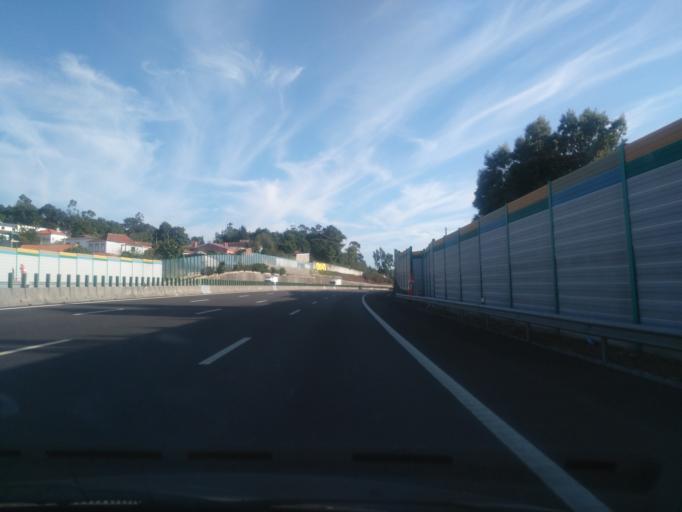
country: PT
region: Porto
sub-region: Vila Nova de Gaia
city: Grijo
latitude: 41.0318
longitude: -8.5722
